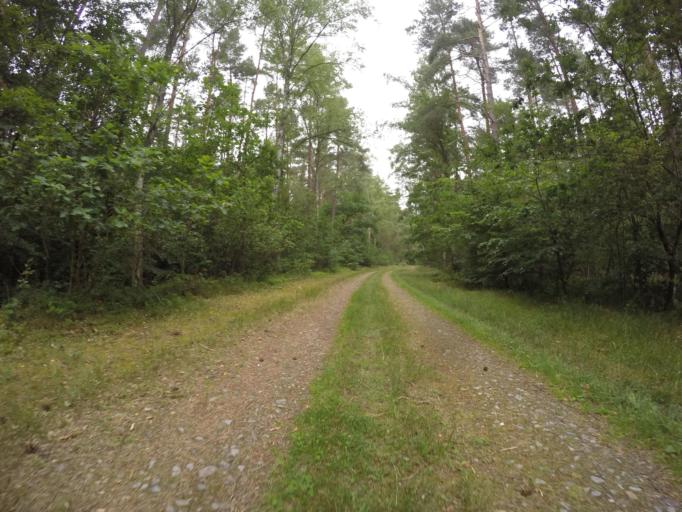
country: DE
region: Lower Saxony
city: Bleckede
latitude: 53.2757
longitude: 10.7129
